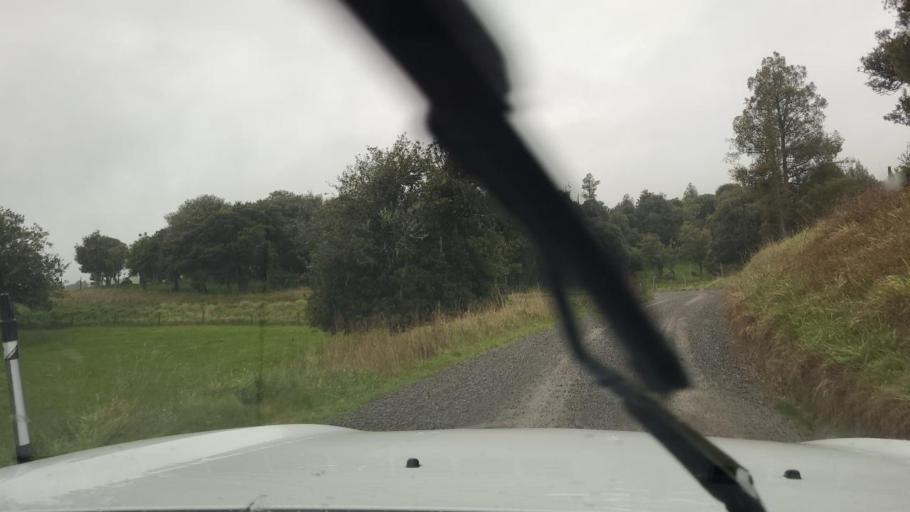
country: NZ
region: Wellington
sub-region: Masterton District
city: Masterton
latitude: -41.0872
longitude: 175.7181
